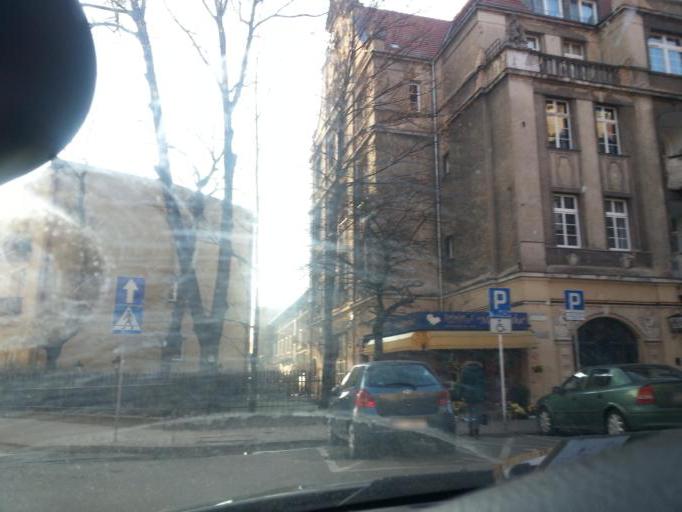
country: PL
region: Lower Silesian Voivodeship
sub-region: Jelenia Gora
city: Jelenia Gora
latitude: 50.9022
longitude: 15.7409
